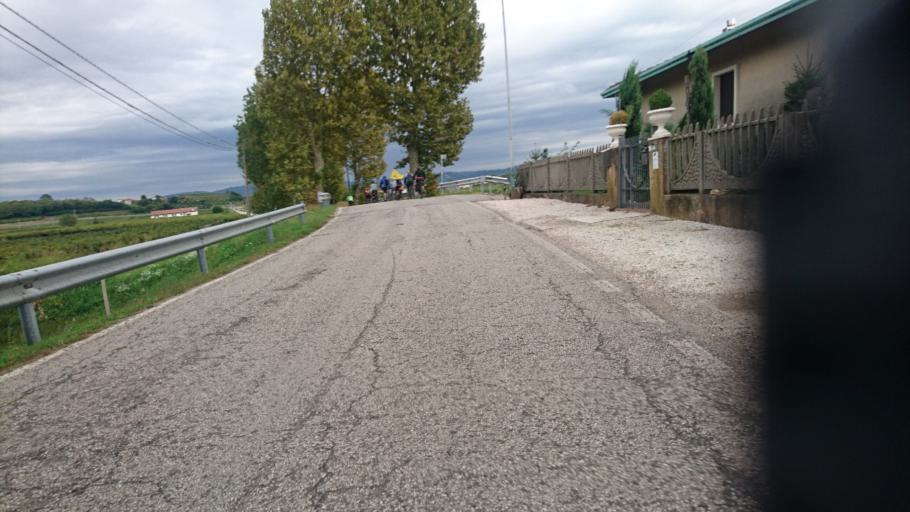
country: IT
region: Veneto
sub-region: Provincia di Vicenza
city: Montebello Vicentino
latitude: 45.4508
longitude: 11.3620
